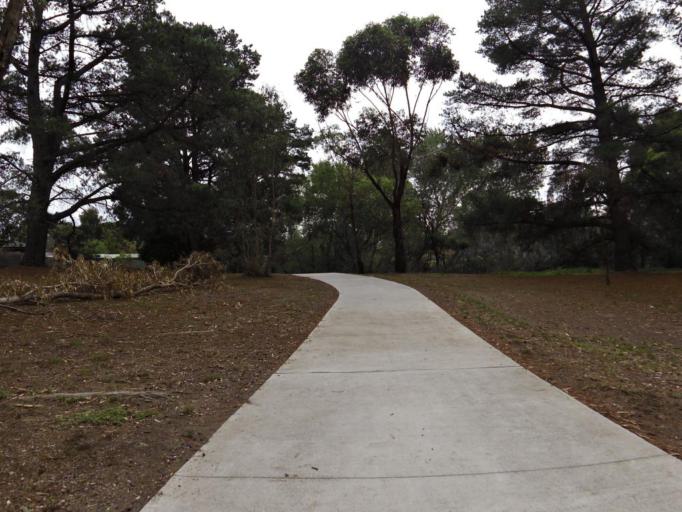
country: AU
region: Victoria
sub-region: Hume
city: Sunbury
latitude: -37.5737
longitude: 144.7195
